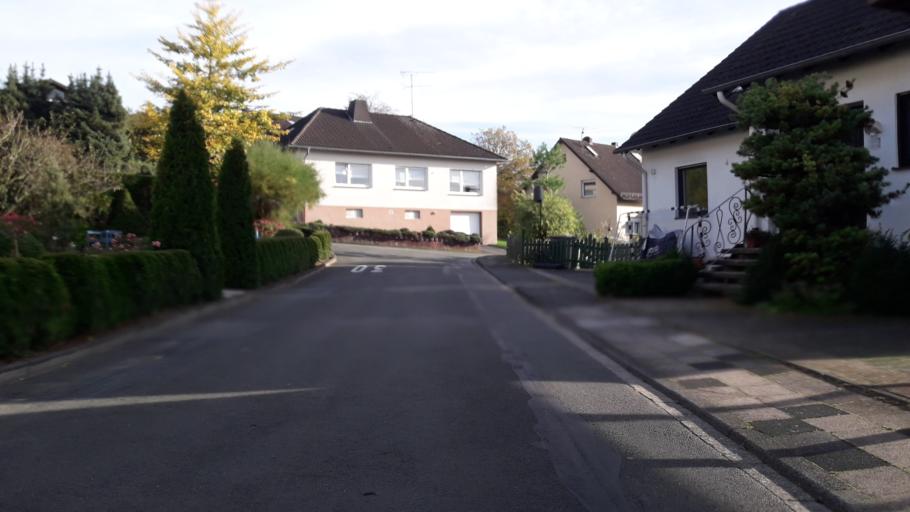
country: DE
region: North Rhine-Westphalia
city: Lichtenau
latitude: 51.6951
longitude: 8.8563
